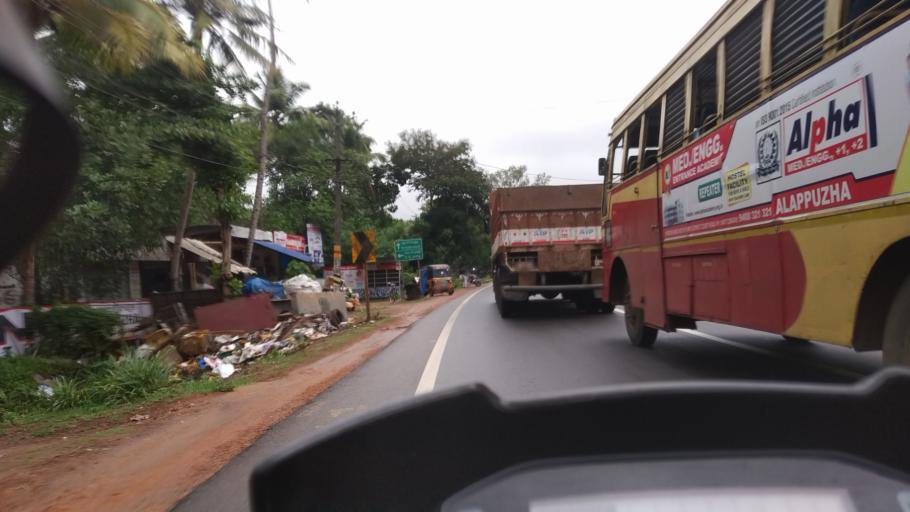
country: IN
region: Kerala
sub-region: Alappuzha
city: Mavelikara
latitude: 9.2934
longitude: 76.4345
